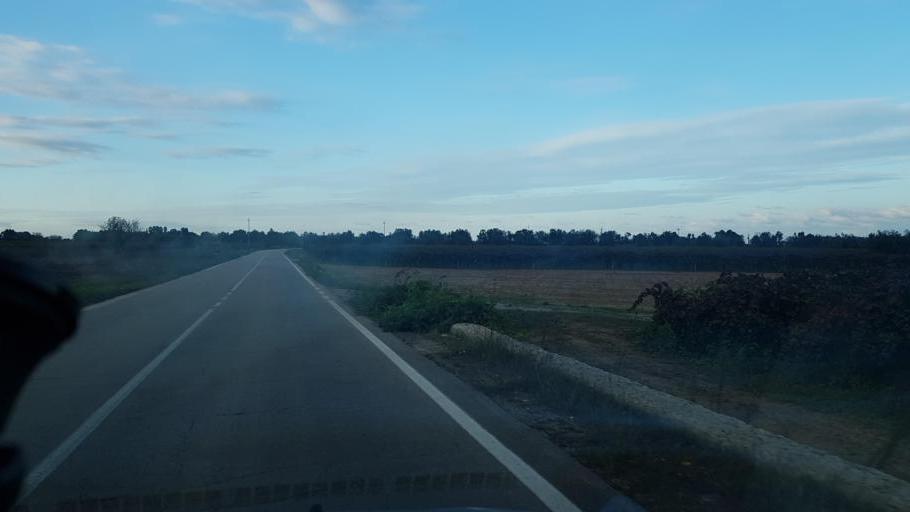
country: IT
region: Apulia
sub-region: Provincia di Lecce
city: Guagnano
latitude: 40.4254
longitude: 17.9505
